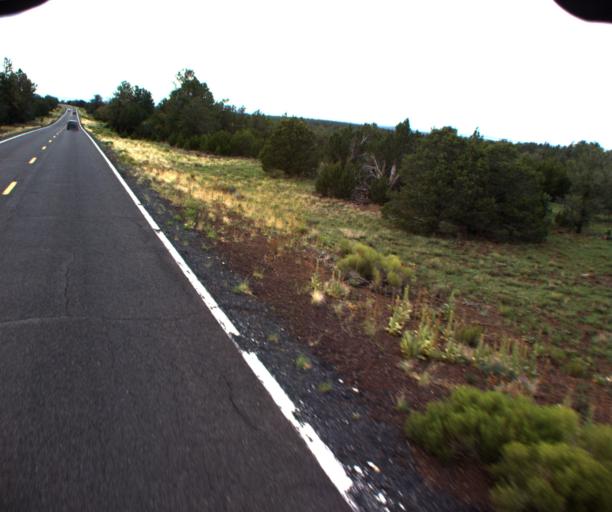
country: US
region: Arizona
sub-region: Coconino County
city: Parks
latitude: 35.5209
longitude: -111.8384
